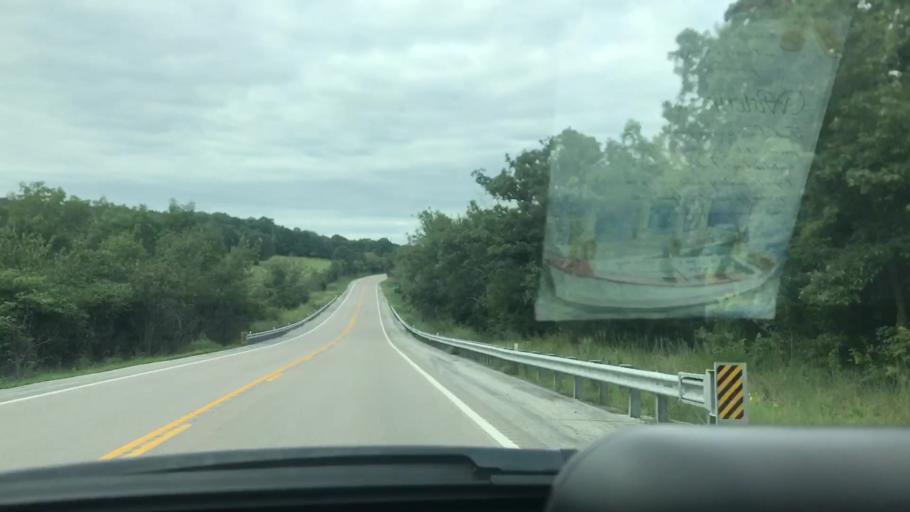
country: US
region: Missouri
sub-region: Benton County
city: Warsaw
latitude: 38.1223
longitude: -93.2783
